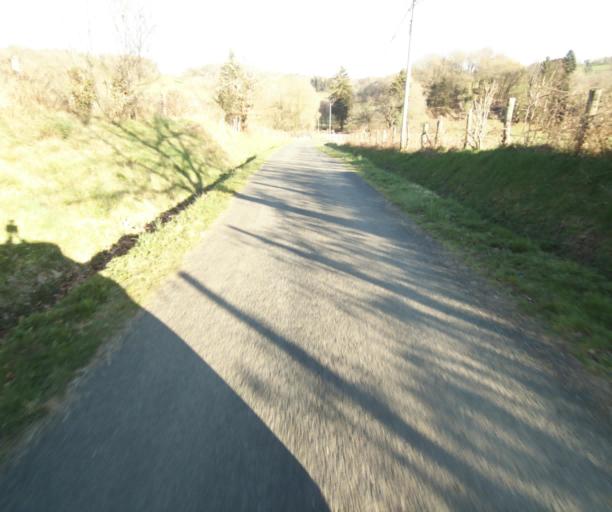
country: FR
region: Limousin
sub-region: Departement de la Correze
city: Saint-Clement
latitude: 45.3636
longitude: 1.6841
